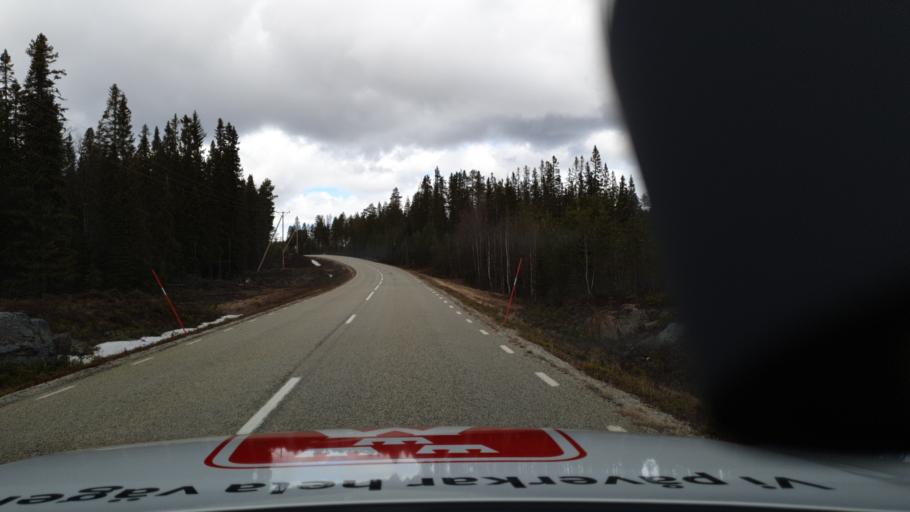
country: SE
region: Jaemtland
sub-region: Are Kommun
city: Jarpen
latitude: 62.7973
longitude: 13.6771
